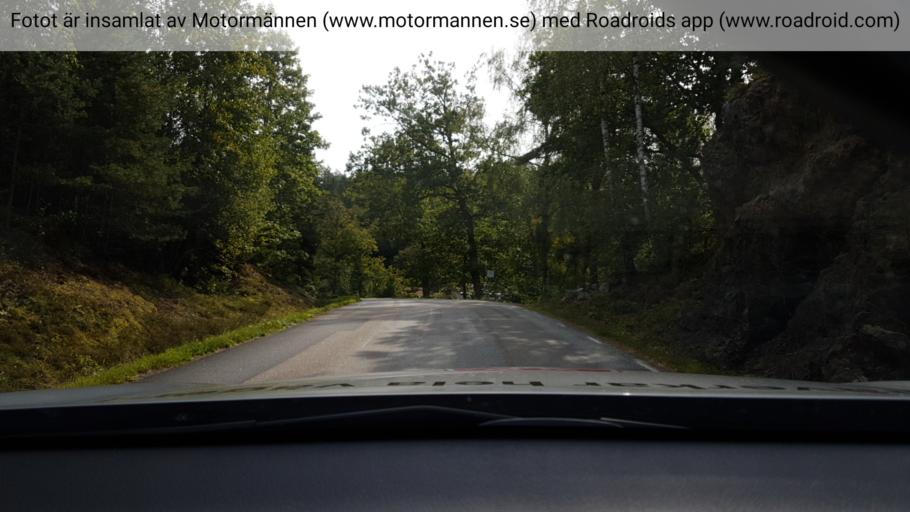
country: SE
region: Vaestra Goetaland
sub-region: Uddevalla Kommun
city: Ljungskile
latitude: 58.2274
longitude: 11.8774
